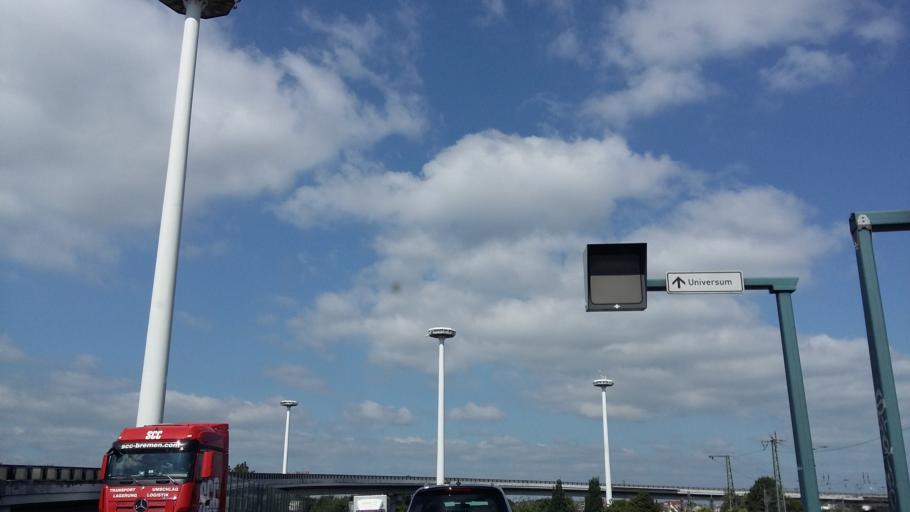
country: DE
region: Bremen
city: Bremen
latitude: 53.0859
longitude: 8.7959
